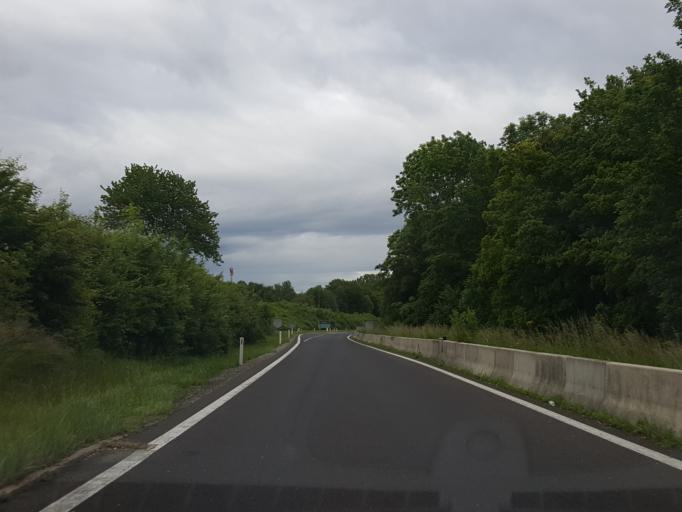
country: AT
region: Upper Austria
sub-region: Politischer Bezirk Vocklabruck
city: Seewalchen
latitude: 47.9520
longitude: 13.5963
